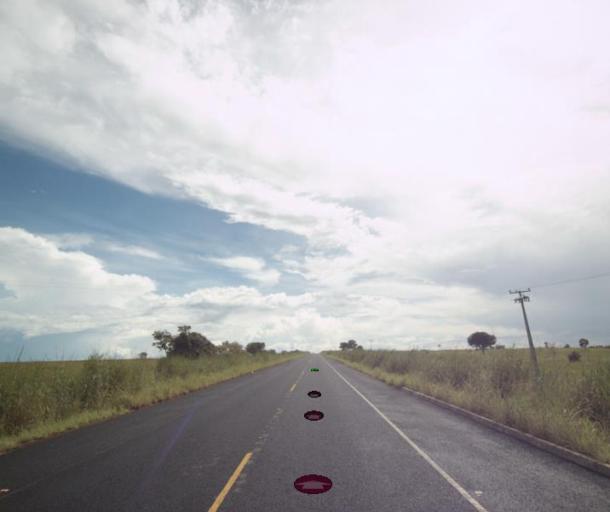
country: BR
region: Goias
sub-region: Sao Miguel Do Araguaia
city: Sao Miguel do Araguaia
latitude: -13.2986
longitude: -50.2501
